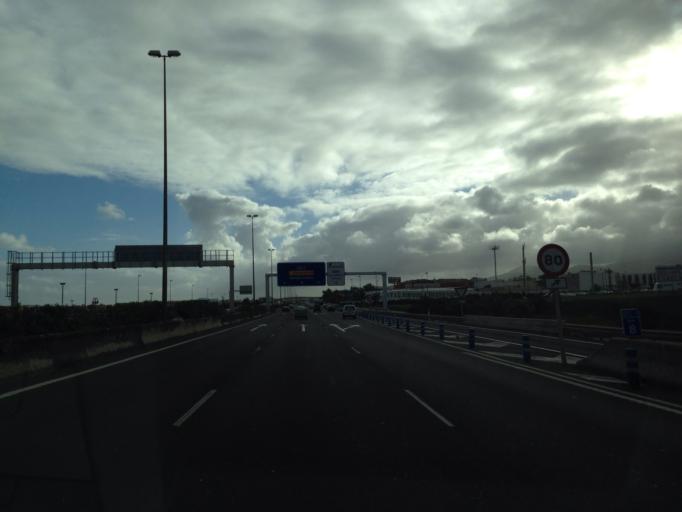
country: ES
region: Canary Islands
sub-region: Provincia de Las Palmas
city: Telde
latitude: 28.0141
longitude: -15.3882
